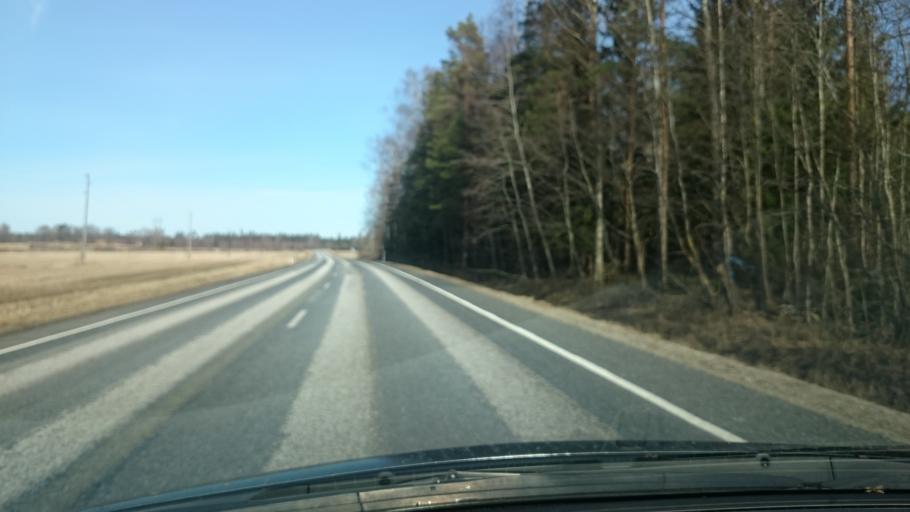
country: EE
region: Jaervamaa
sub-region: Tueri vald
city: Sarevere
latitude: 58.7234
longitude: 25.2821
